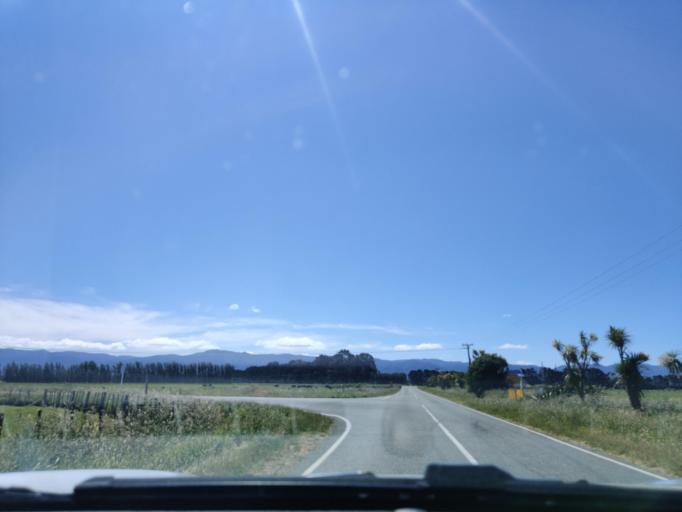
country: NZ
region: Wellington
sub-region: Upper Hutt City
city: Upper Hutt
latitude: -41.2836
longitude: 175.2675
